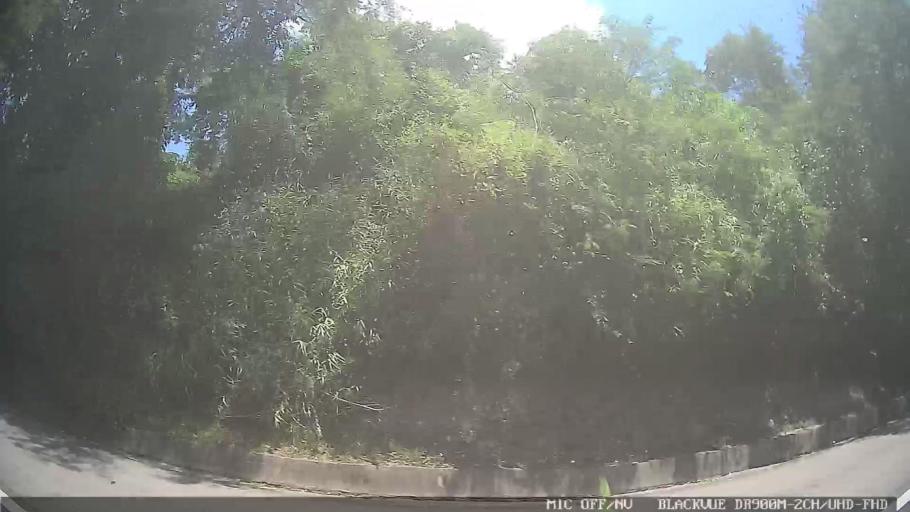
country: BR
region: Sao Paulo
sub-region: Caraguatatuba
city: Caraguatatuba
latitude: -23.4829
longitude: -45.5758
